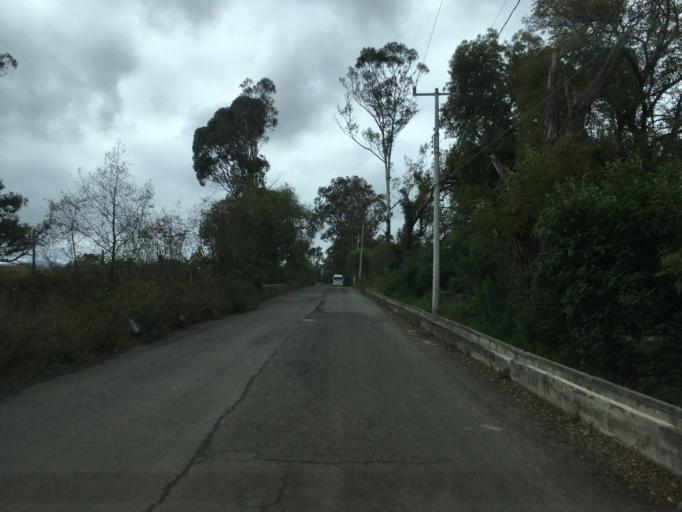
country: MX
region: Hidalgo
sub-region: Omitlan de Juarez
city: San Antonio el Paso
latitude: 20.2263
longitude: -98.5783
